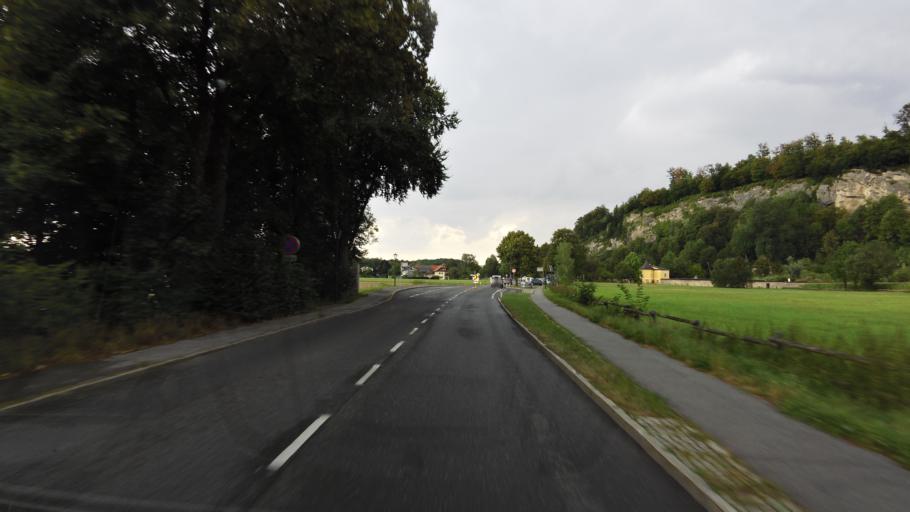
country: AT
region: Salzburg
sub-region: Politischer Bezirk Salzburg-Umgebung
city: Anif
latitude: 47.7548
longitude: 13.0639
